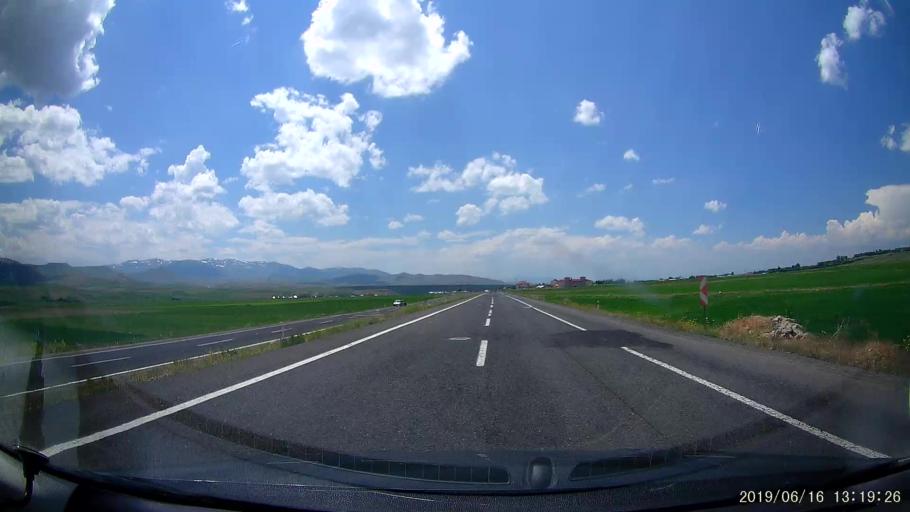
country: TR
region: Agri
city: Taslicay
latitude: 39.6328
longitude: 43.4068
